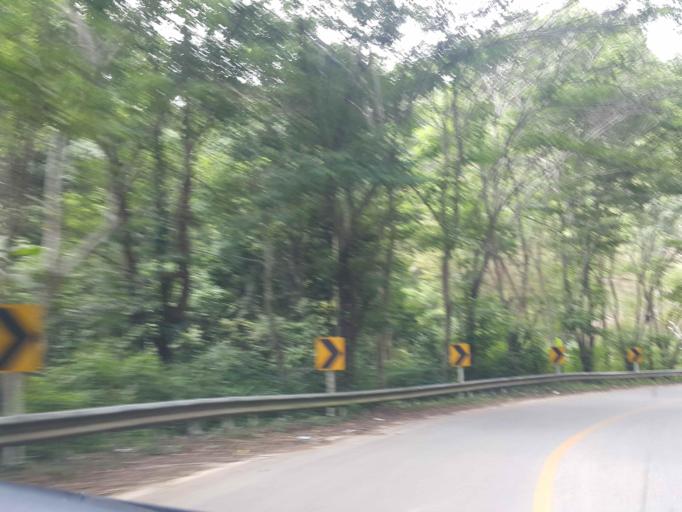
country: TH
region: Chiang Mai
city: Samoeng
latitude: 18.8764
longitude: 98.7954
